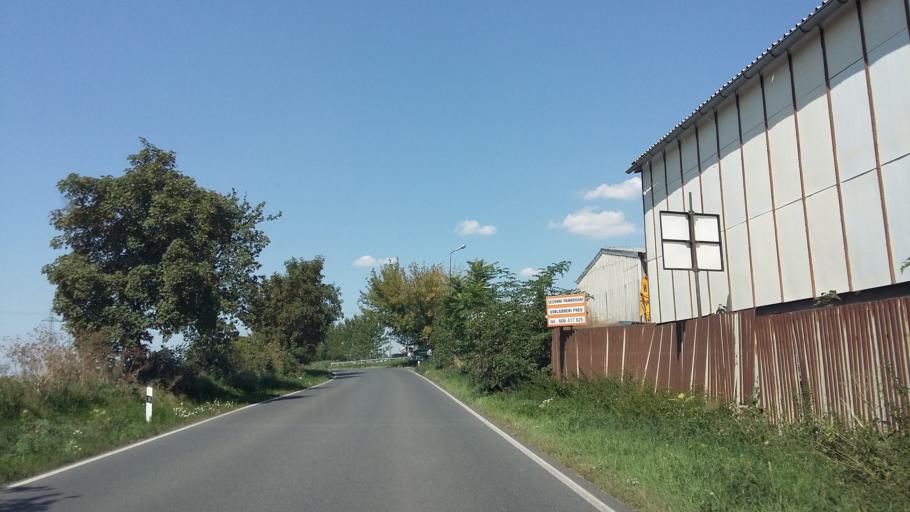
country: CZ
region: Central Bohemia
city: Jirny
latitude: 50.1433
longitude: 14.6924
